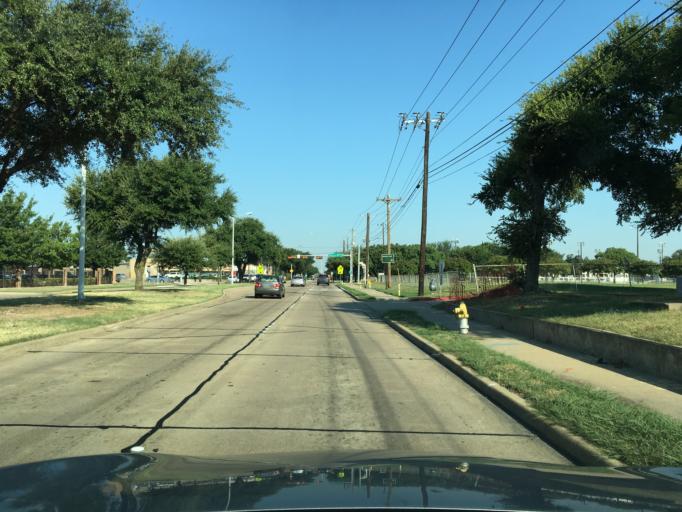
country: US
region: Texas
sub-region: Dallas County
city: Garland
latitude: 32.9509
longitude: -96.6526
